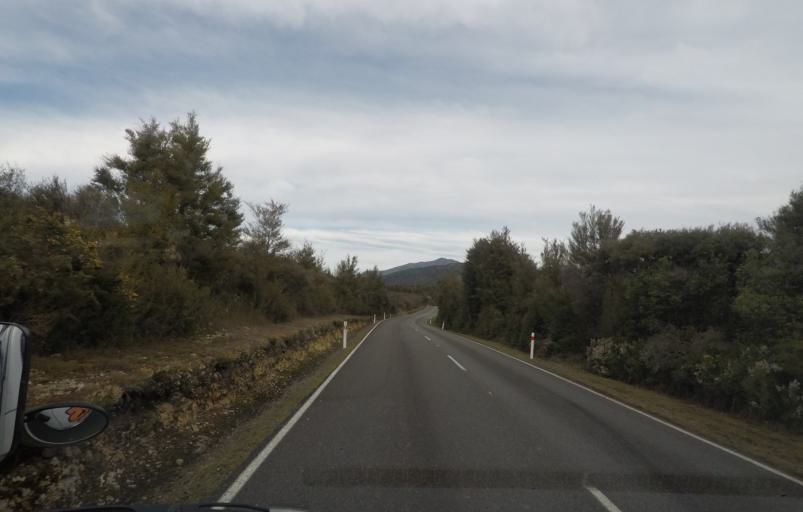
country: NZ
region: Tasman
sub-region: Tasman District
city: Takaka
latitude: -40.8440
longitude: 172.7748
